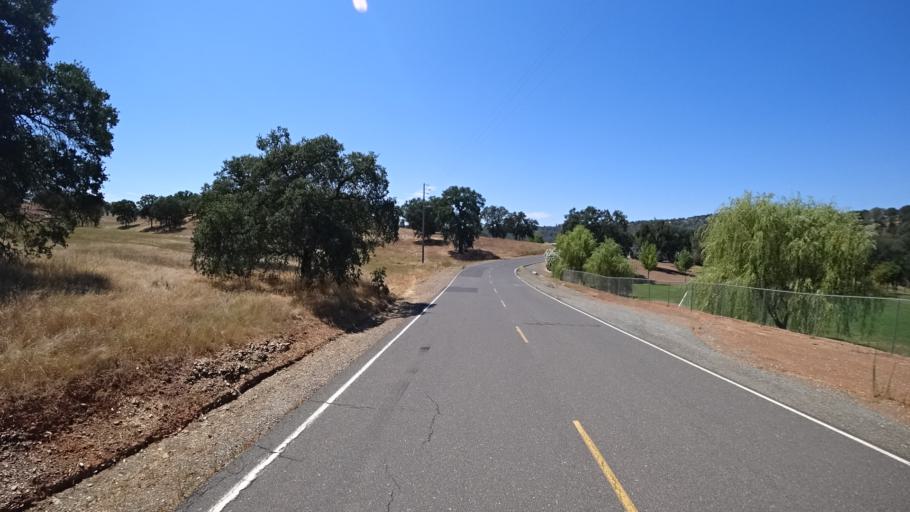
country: US
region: California
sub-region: Calaveras County
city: Copperopolis
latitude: 37.9404
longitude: -120.6201
